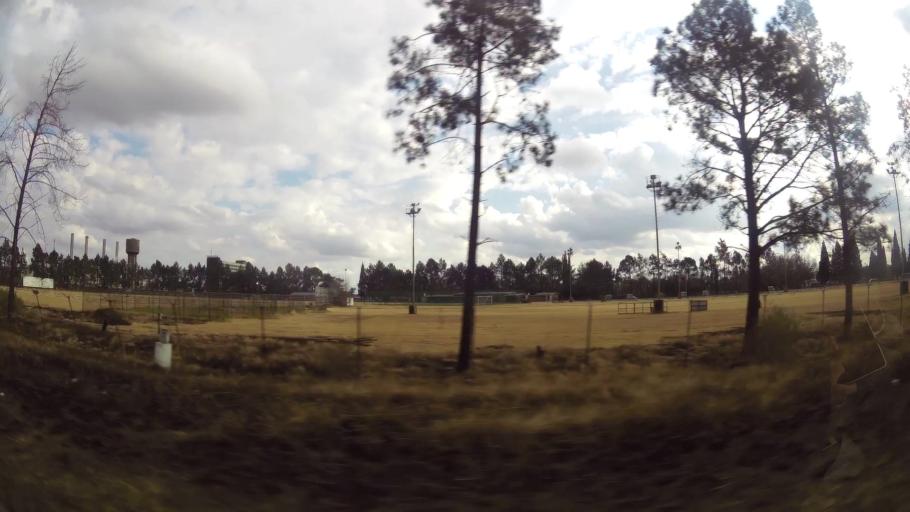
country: ZA
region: Orange Free State
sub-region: Fezile Dabi District Municipality
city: Sasolburg
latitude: -26.8159
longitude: 27.8418
